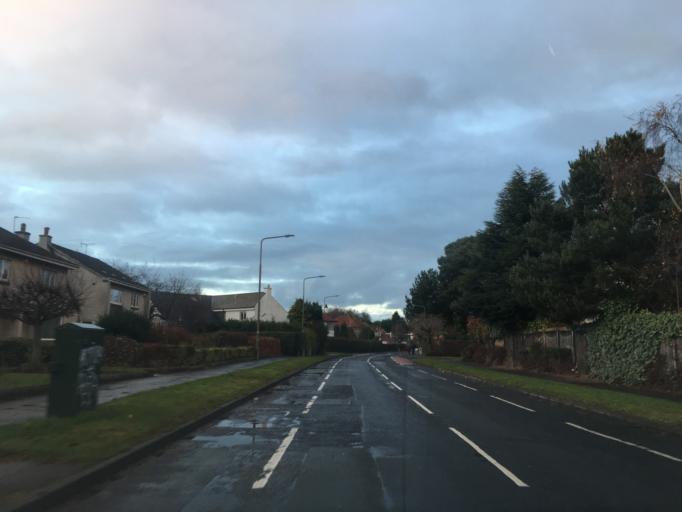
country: GB
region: Scotland
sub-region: Edinburgh
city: Colinton
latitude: 55.9593
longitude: -3.2697
